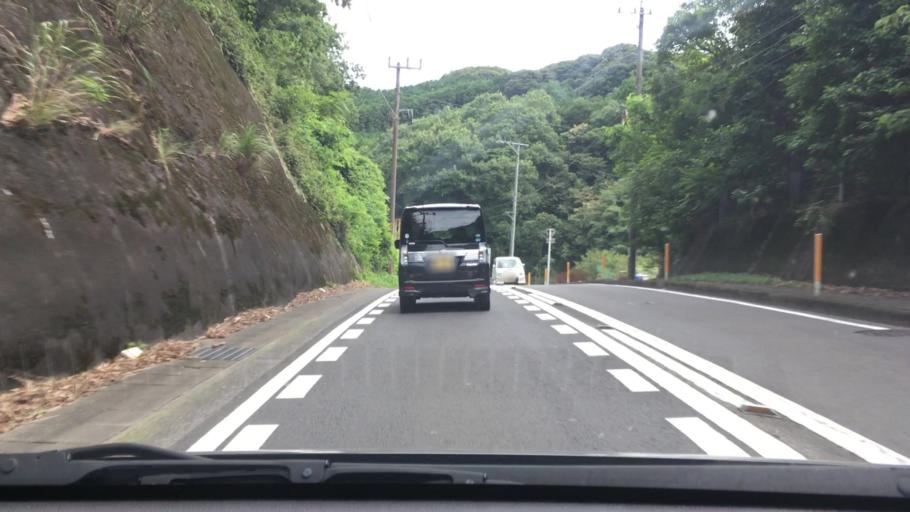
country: JP
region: Nagasaki
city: Togitsu
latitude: 32.9297
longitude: 129.7825
